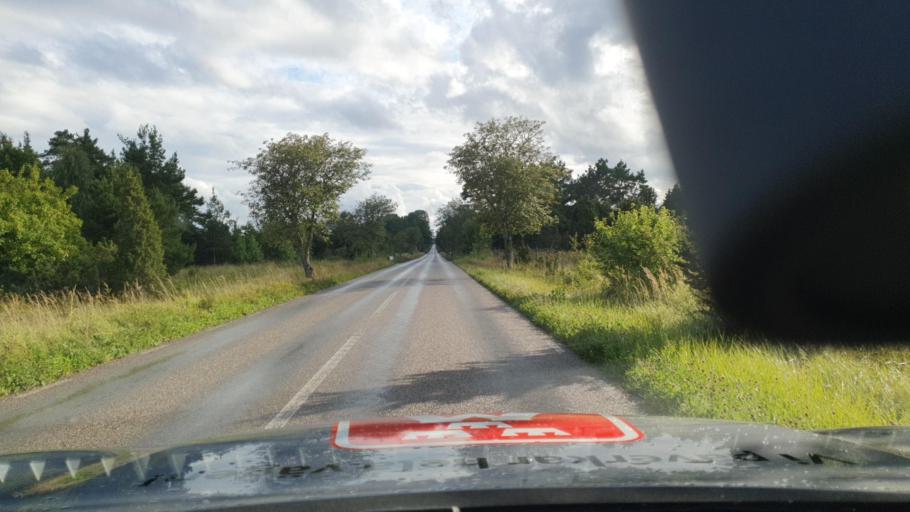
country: SE
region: Gotland
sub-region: Gotland
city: Slite
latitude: 57.6464
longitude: 18.7689
